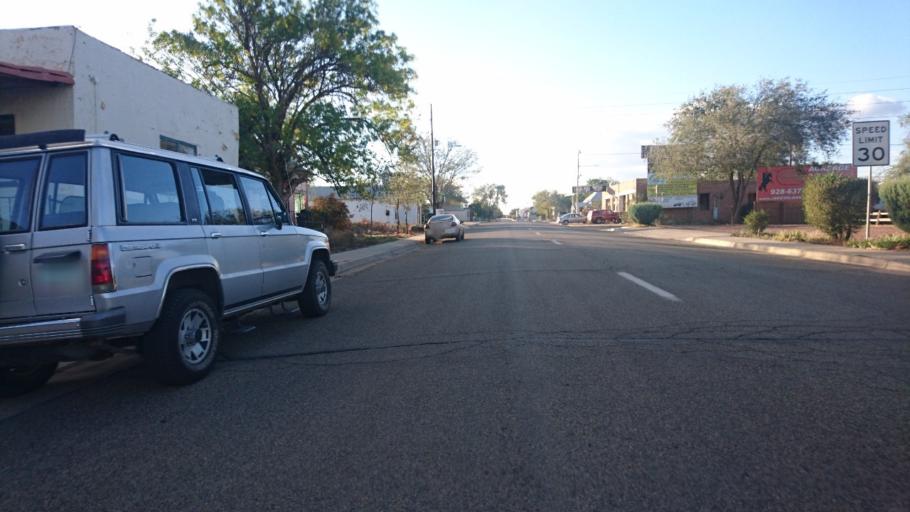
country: US
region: Arizona
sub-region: Coconino County
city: Williams
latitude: 35.2236
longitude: -112.4802
